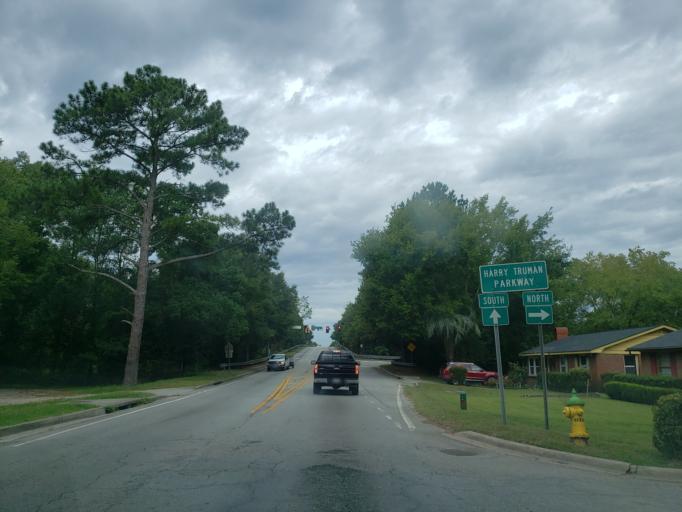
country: US
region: Georgia
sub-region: Chatham County
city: Thunderbolt
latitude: 32.0339
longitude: -81.0806
